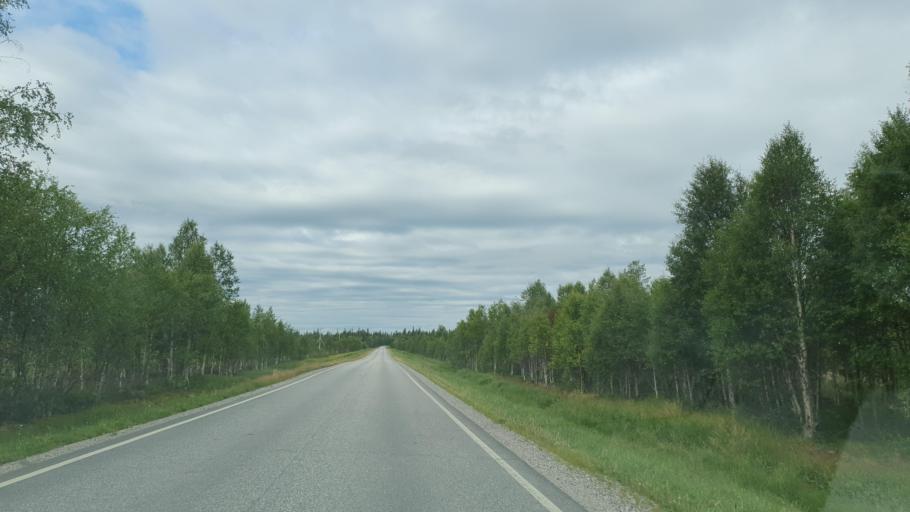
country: FI
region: Lapland
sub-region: Tunturi-Lappi
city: Kittilae
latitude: 67.5774
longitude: 25.6084
